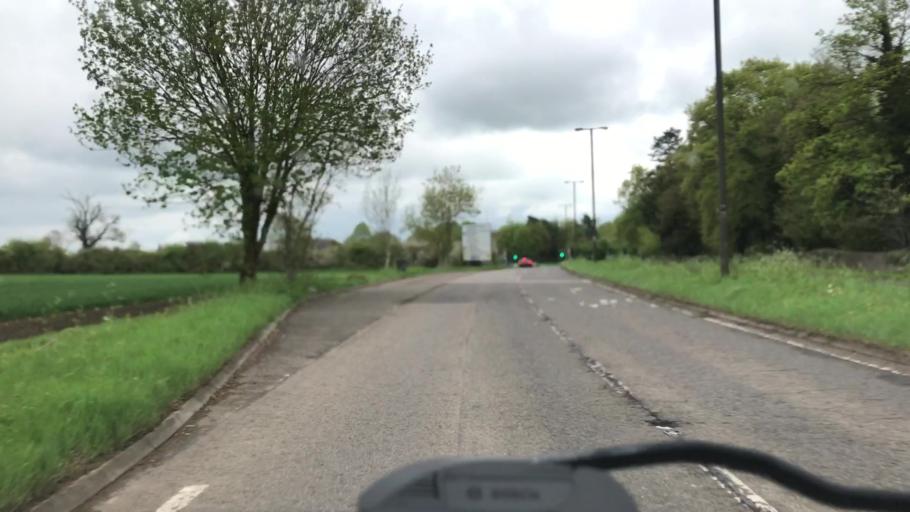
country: GB
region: England
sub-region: Gloucestershire
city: Cirencester
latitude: 51.7192
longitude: -1.9613
